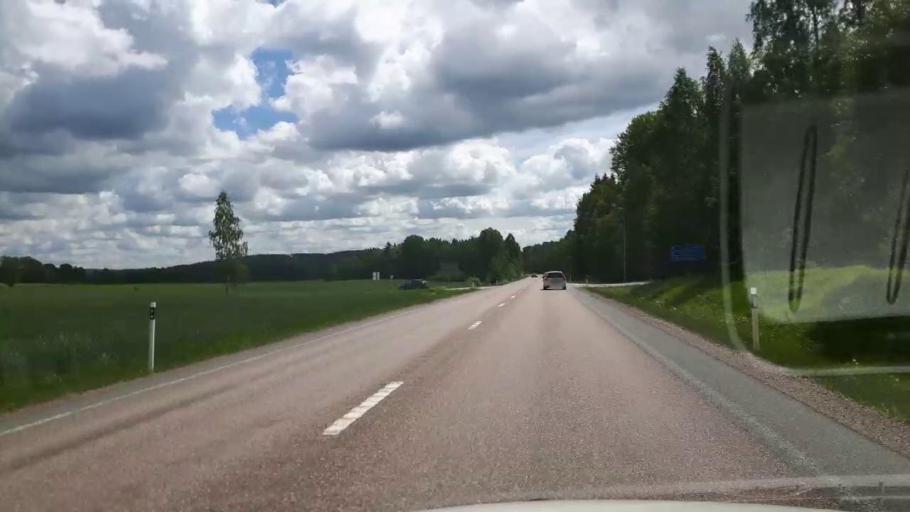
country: SE
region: Dalarna
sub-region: Saters Kommun
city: Saeter
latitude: 60.4796
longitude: 15.7779
